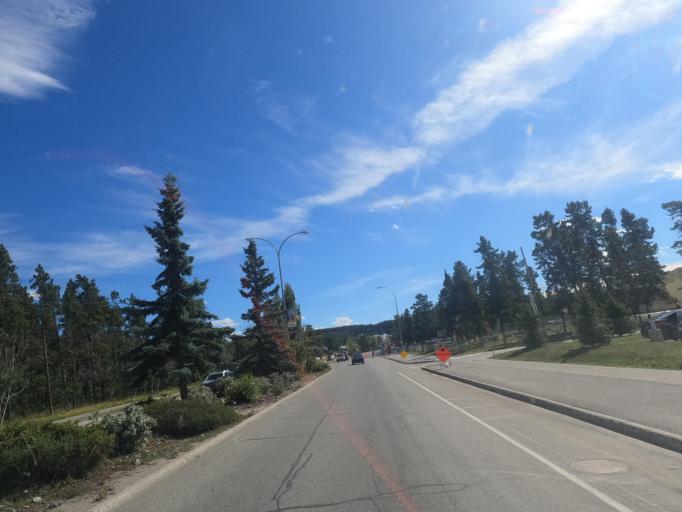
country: CA
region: Yukon
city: Whitehorse
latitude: 60.7096
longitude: -135.0372
